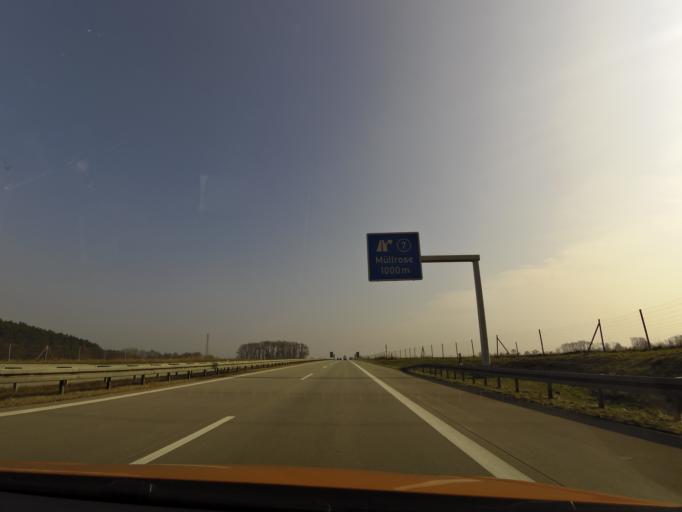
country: DE
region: Brandenburg
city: Jacobsdorf
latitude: 52.3227
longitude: 14.3298
